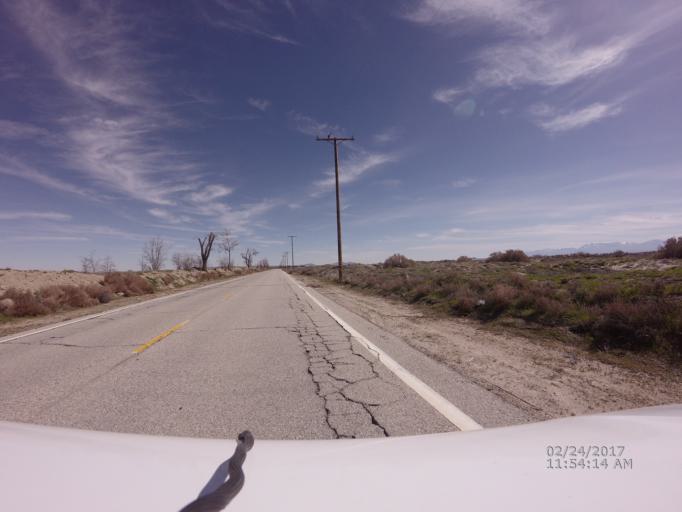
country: US
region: California
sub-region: Los Angeles County
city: Lancaster
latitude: 34.7191
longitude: -118.0355
